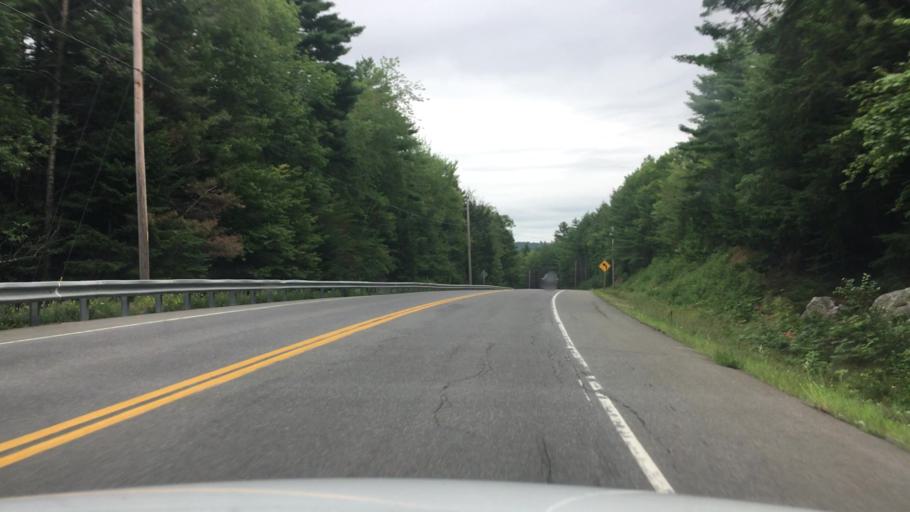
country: US
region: Maine
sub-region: Penobscot County
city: Bradley
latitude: 44.8257
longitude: -68.4115
